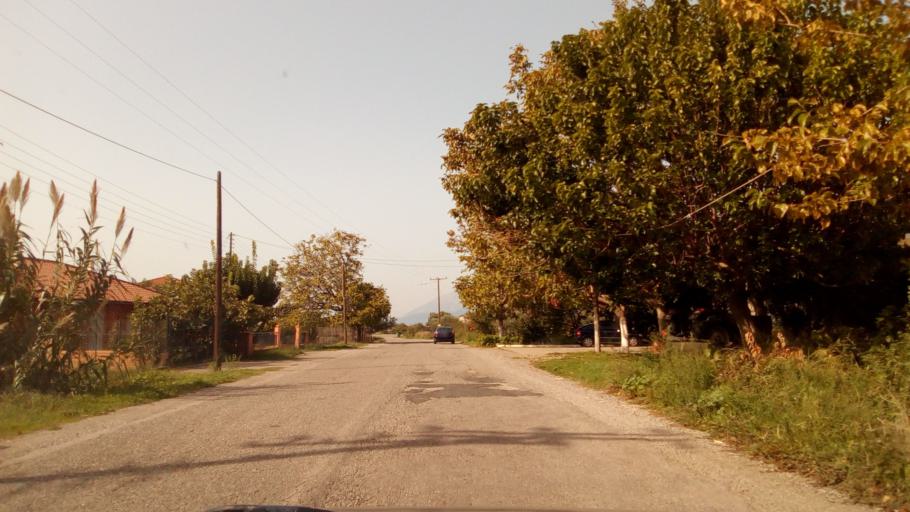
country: GR
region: West Greece
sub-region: Nomos Aitolias kai Akarnanias
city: Nafpaktos
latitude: 38.3953
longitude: 21.8861
